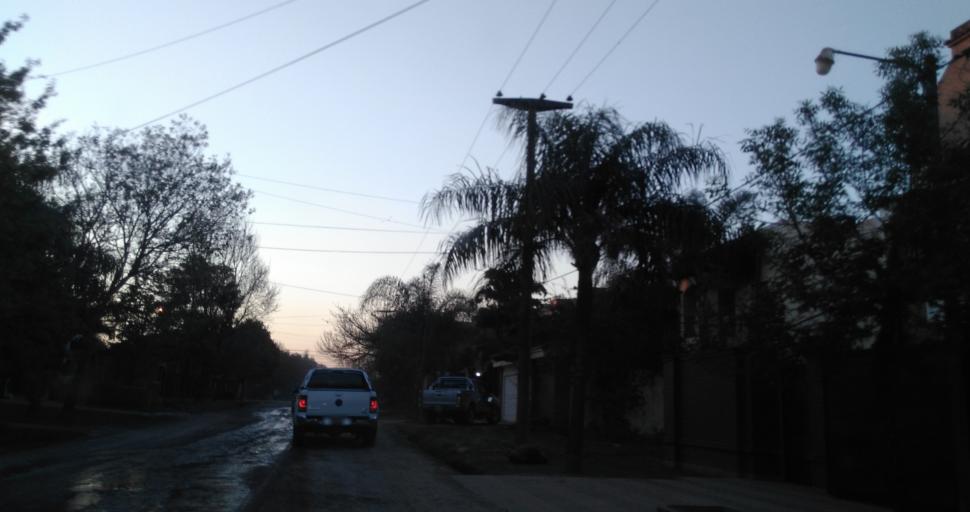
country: AR
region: Chaco
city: Resistencia
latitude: -27.4390
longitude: -58.9663
